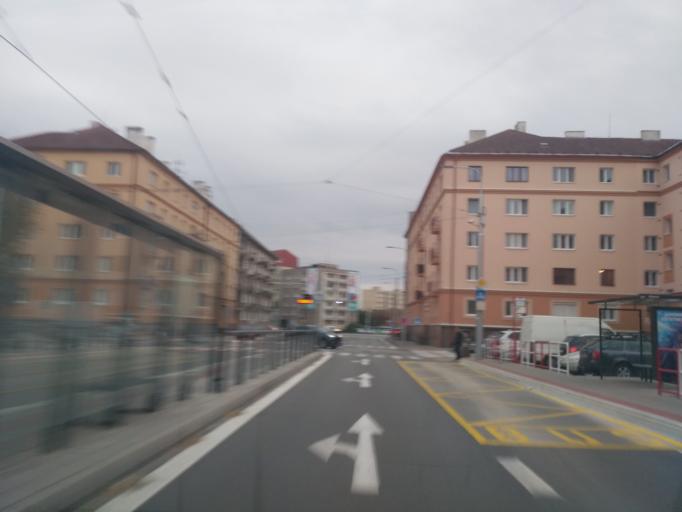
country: SK
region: Kosicky
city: Kosice
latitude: 48.7282
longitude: 21.2465
